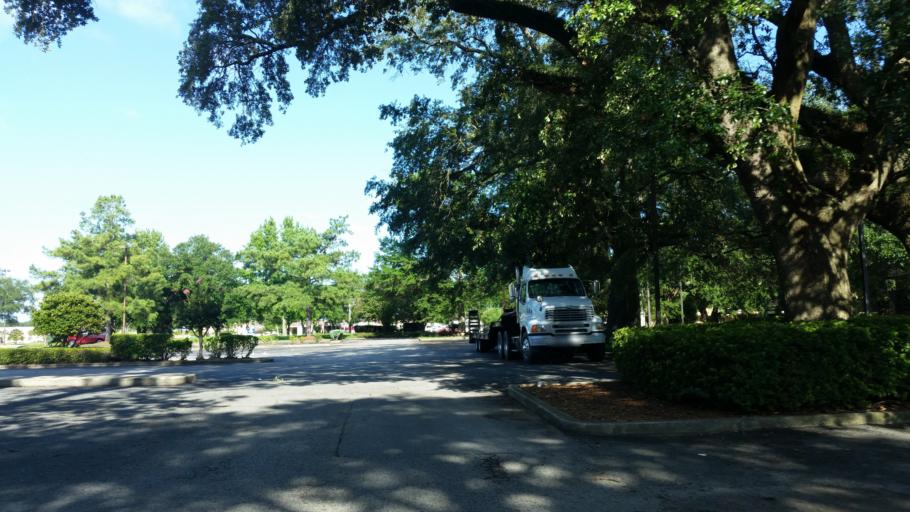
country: US
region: Florida
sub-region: Escambia County
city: Ferry Pass
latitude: 30.5020
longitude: -87.2229
